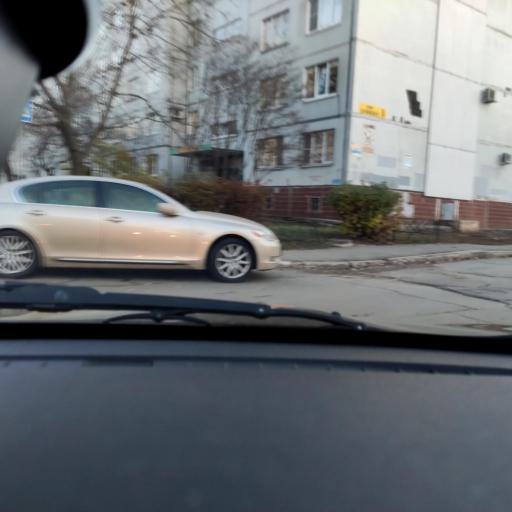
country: RU
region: Samara
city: Tol'yatti
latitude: 53.5318
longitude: 49.3338
